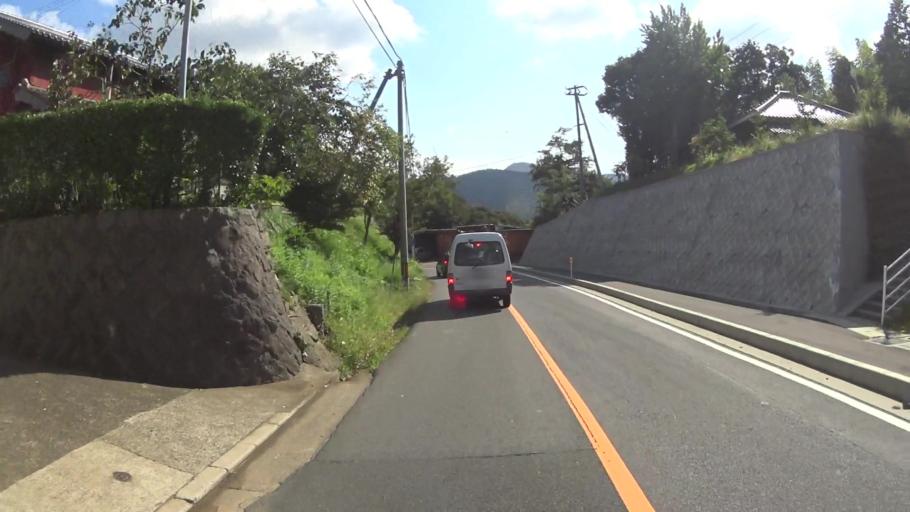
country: JP
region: Kyoto
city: Miyazu
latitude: 35.7508
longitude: 135.1672
